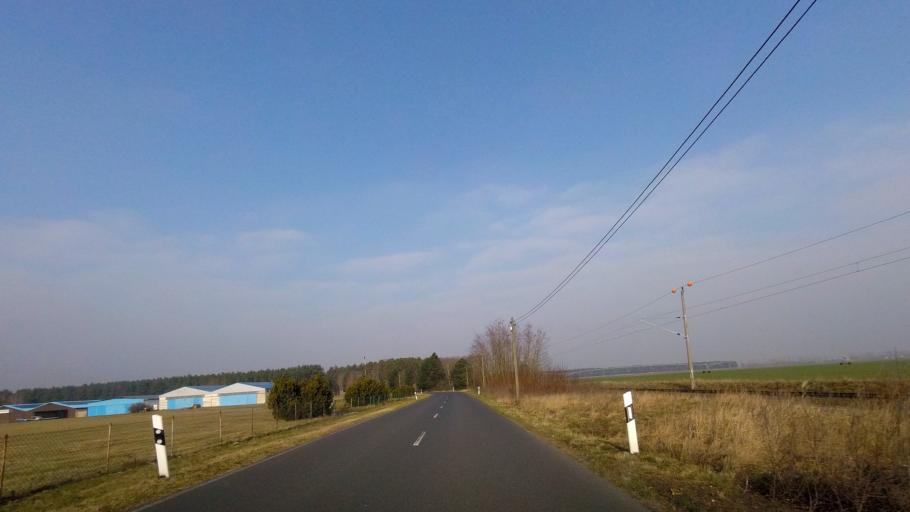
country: DE
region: Brandenburg
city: Juterbog
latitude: 51.9002
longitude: 13.0638
